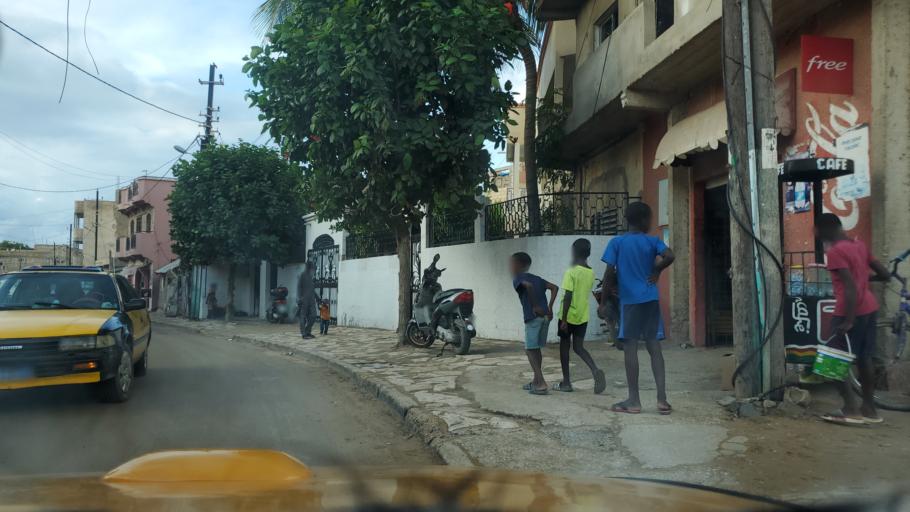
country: SN
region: Dakar
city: Mermoz Boabab
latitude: 14.7209
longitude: -17.4895
